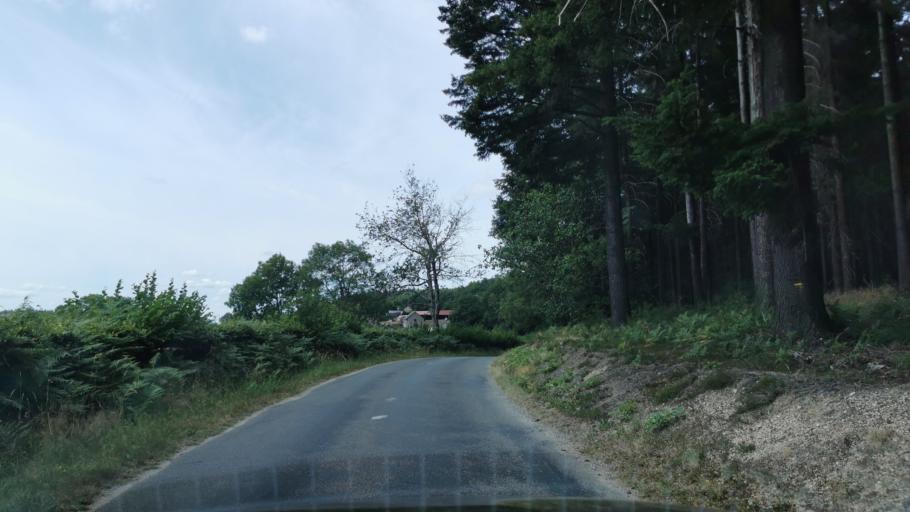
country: FR
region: Bourgogne
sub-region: Departement de Saone-et-Loire
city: Marmagne
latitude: 46.8096
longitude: 4.2853
